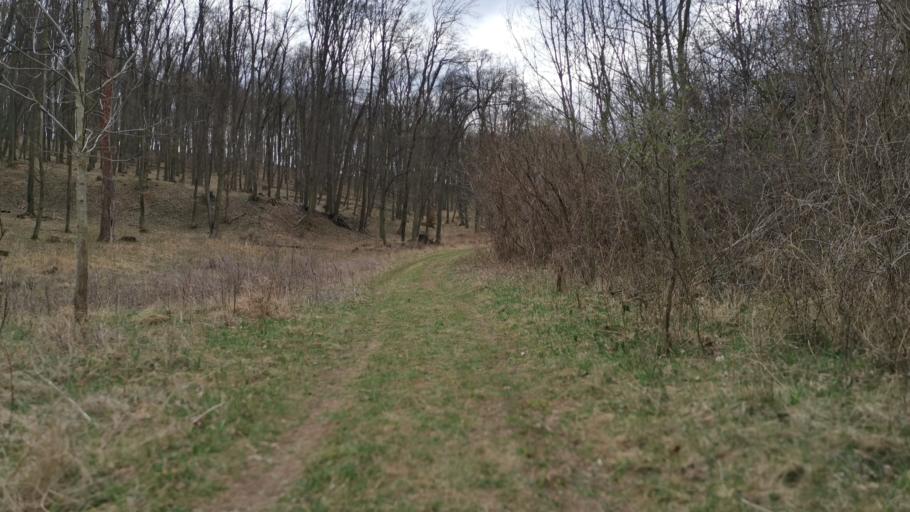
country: CZ
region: South Moravian
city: Petrov
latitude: 48.8438
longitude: 17.3142
